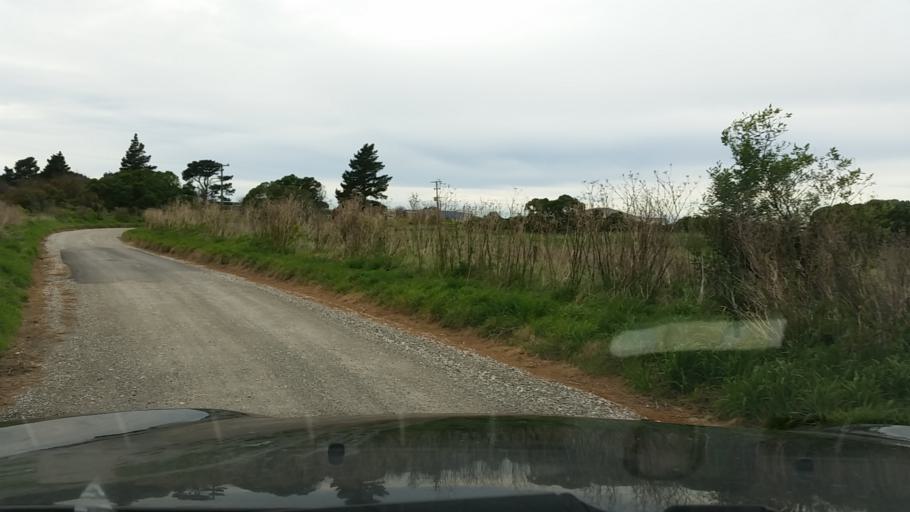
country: NZ
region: Marlborough
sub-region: Marlborough District
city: Blenheim
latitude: -41.9241
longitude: 174.0913
